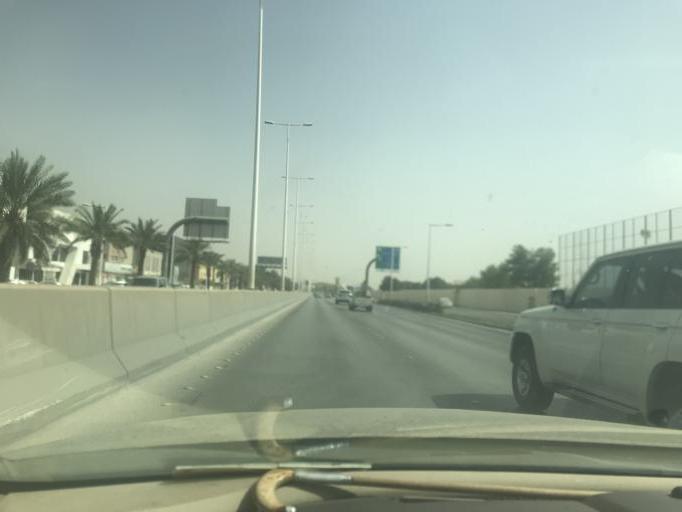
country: SA
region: Ar Riyad
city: Riyadh
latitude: 24.7371
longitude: 46.7068
